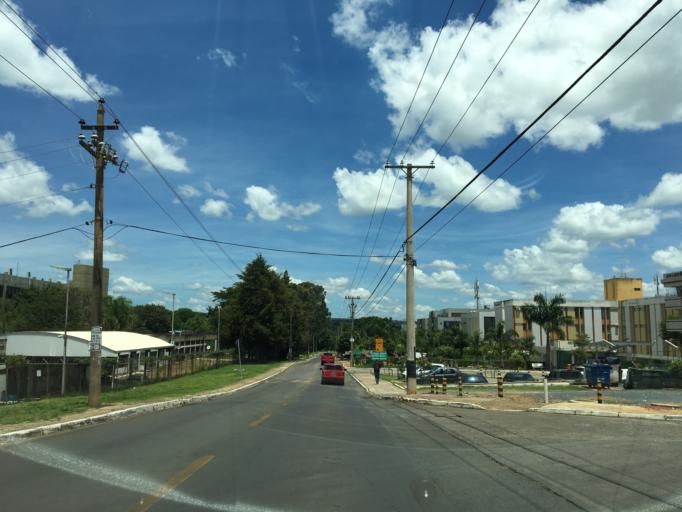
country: BR
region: Federal District
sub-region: Brasilia
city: Brasilia
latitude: -15.7324
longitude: -47.8988
